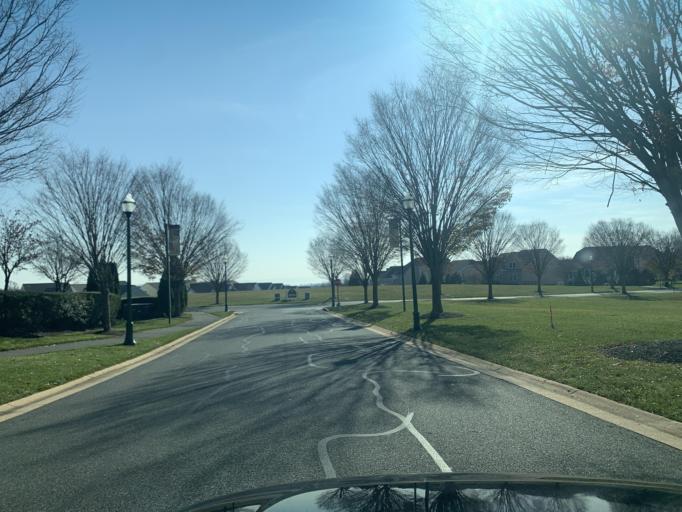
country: US
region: Maryland
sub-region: Harford County
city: Havre de Grace
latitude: 39.5531
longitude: -76.1284
